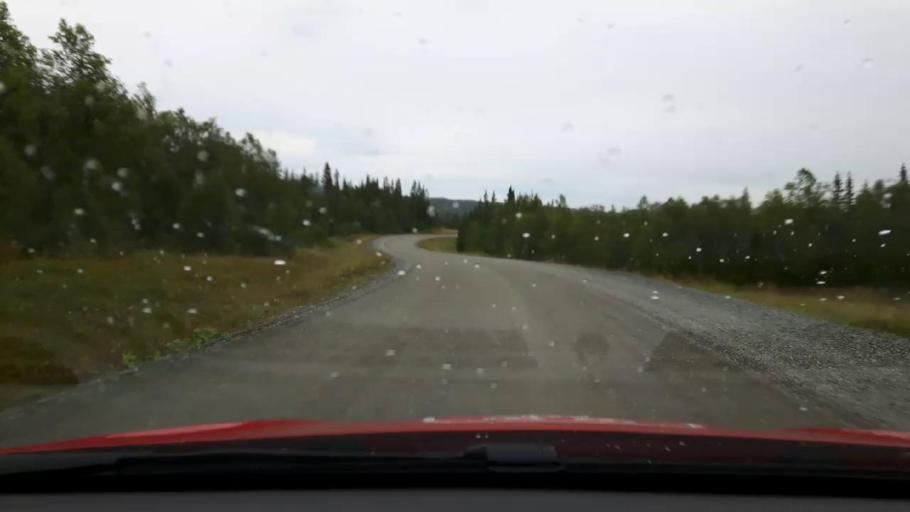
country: SE
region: Jaemtland
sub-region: Are Kommun
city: Are
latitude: 63.5136
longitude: 12.4209
